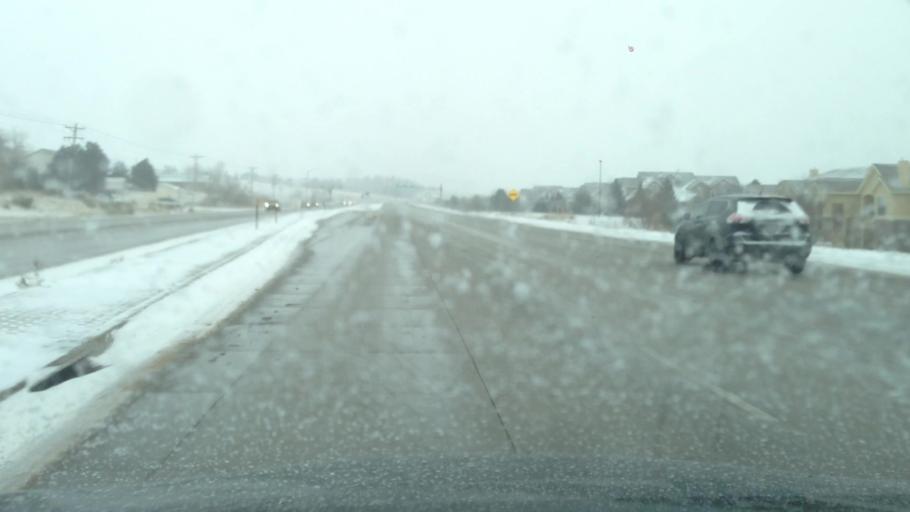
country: US
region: Colorado
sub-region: Arapahoe County
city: Dove Valley
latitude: 39.5876
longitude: -104.7980
